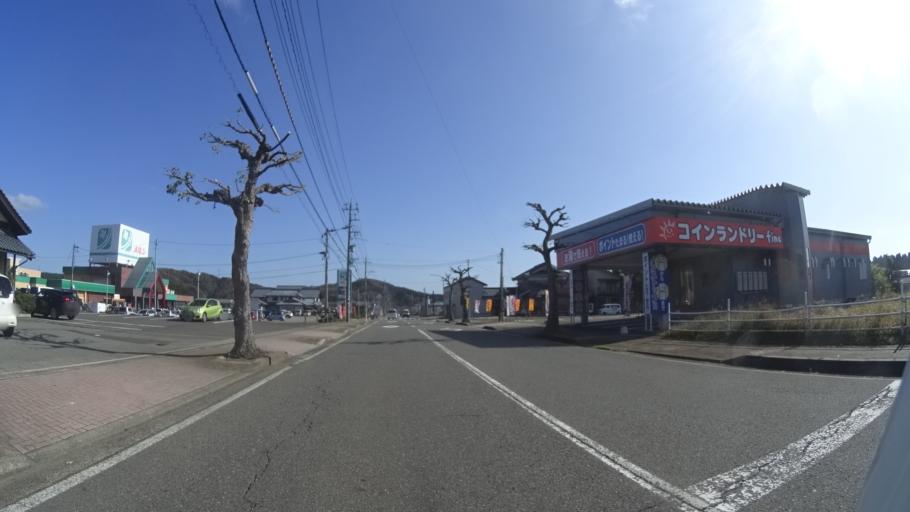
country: JP
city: Asahi
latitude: 35.9614
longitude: 136.0526
